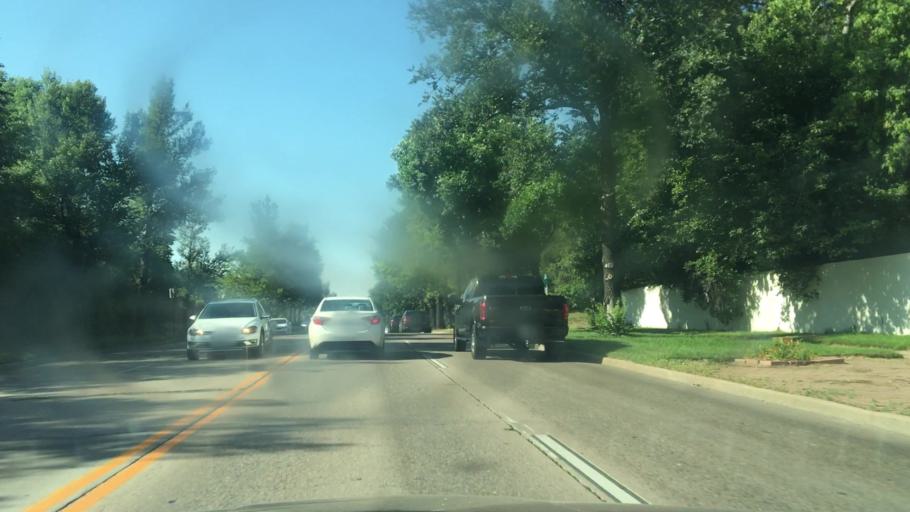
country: US
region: Colorado
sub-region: Arapahoe County
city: Glendale
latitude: 39.7098
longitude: -104.9594
